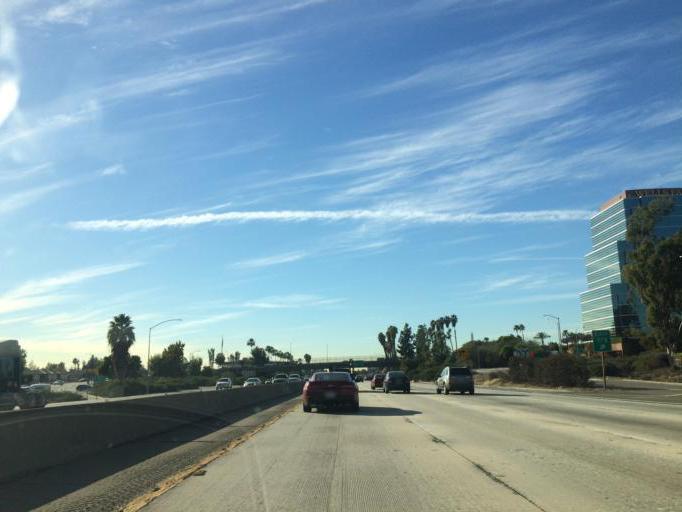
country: US
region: California
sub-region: Los Angeles County
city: Covina
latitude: 34.0719
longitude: -117.8780
